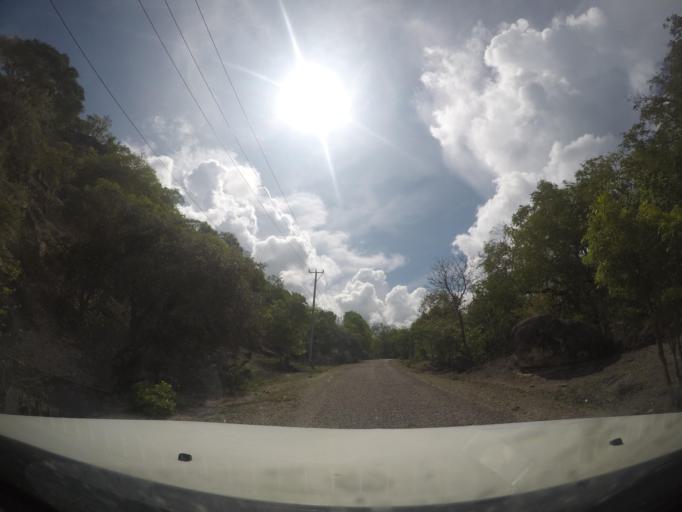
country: TL
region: Lautem
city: Lospalos
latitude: -8.3434
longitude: 127.0367
